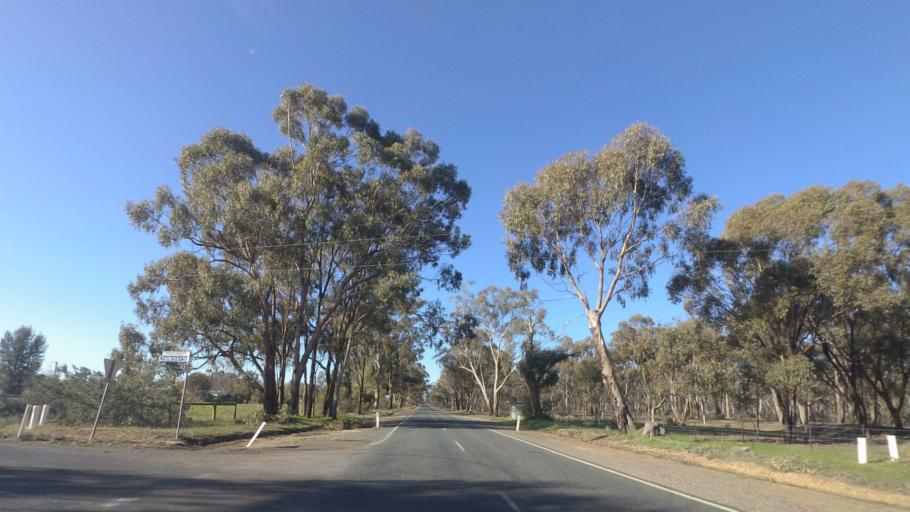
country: AU
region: Victoria
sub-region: Greater Bendigo
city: Epsom
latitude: -36.6742
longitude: 144.4002
